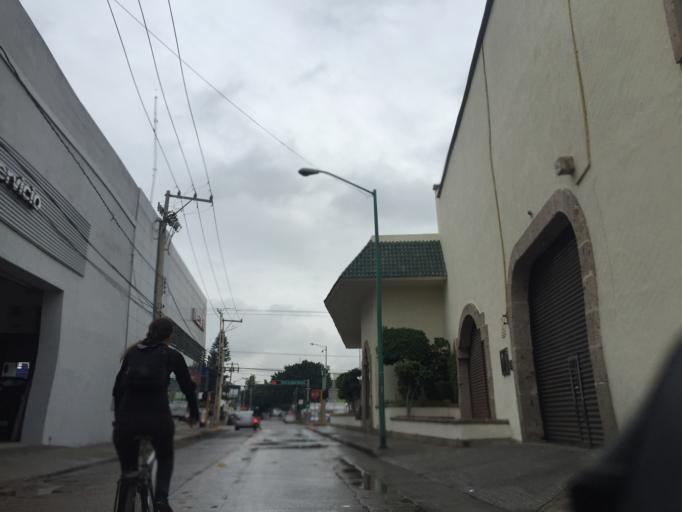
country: MX
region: Guanajuato
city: Leon
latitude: 21.1193
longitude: -101.6677
